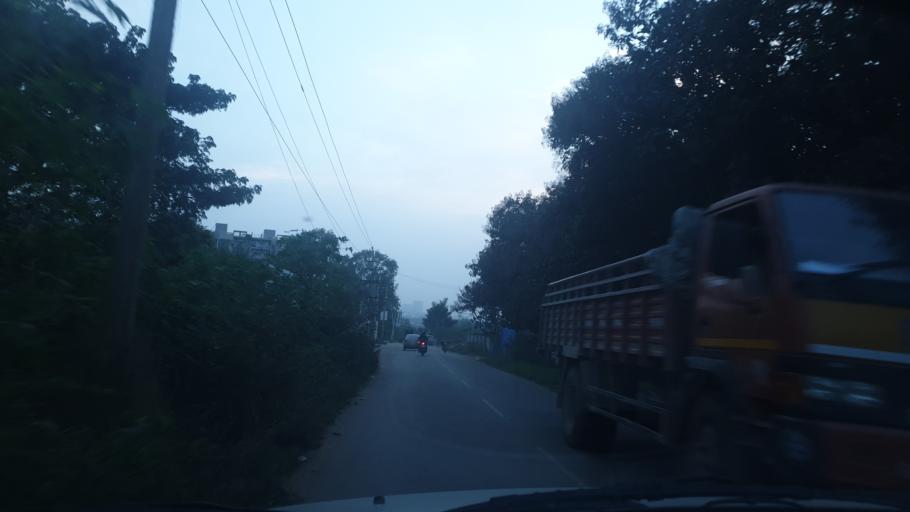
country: IN
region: Karnataka
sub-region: Bangalore Urban
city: Yelahanka
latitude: 13.0572
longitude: 77.6837
